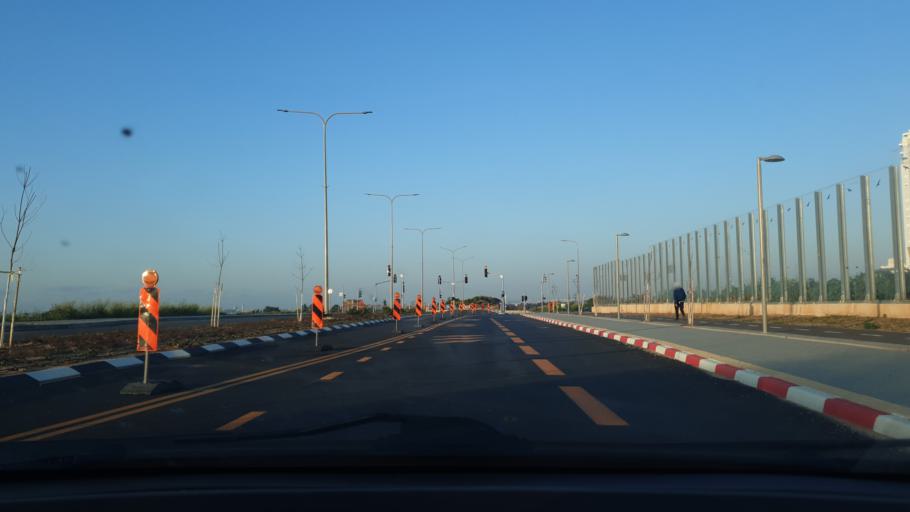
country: IL
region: Central District
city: Ramla
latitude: 31.9364
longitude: 34.8521
